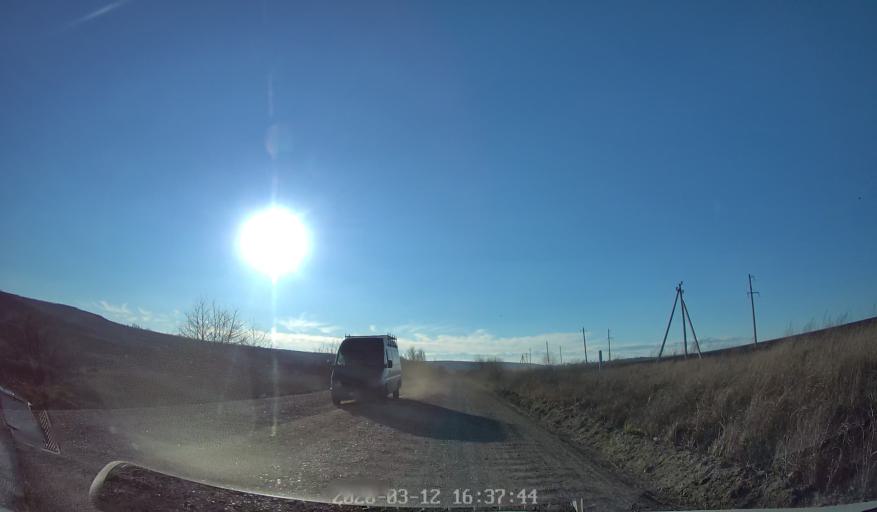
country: MD
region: Anenii Noi
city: Anenii Noi
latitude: 46.8154
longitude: 29.1857
